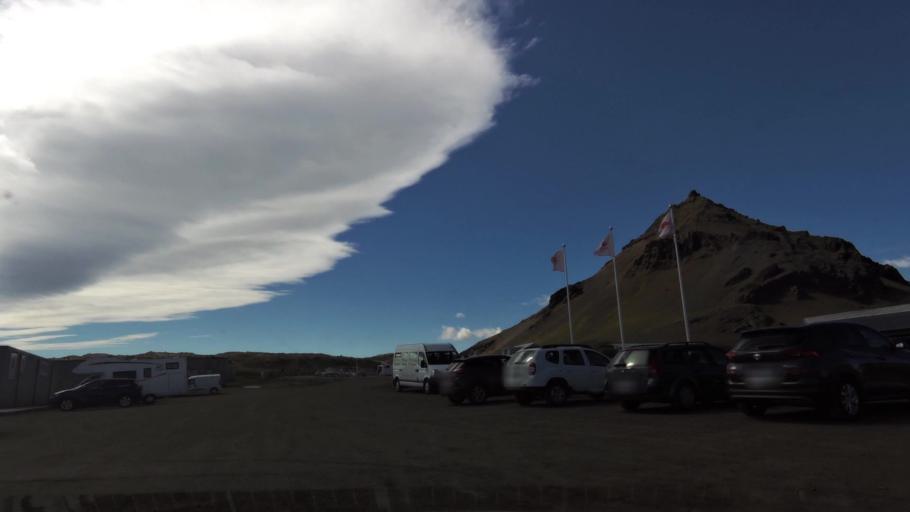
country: IS
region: West
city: Olafsvik
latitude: 64.7673
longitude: -23.6292
